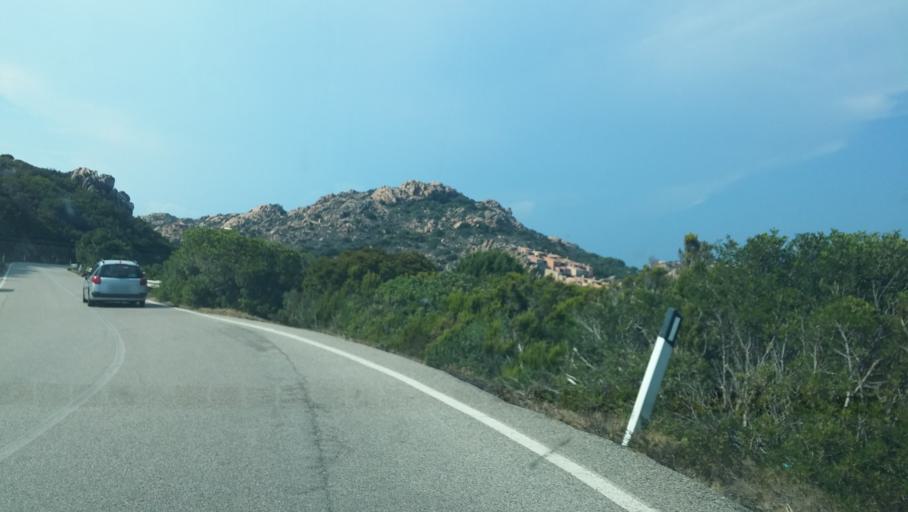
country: IT
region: Sardinia
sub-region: Provincia di Olbia-Tempio
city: La Maddalena
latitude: 41.2555
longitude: 9.4283
